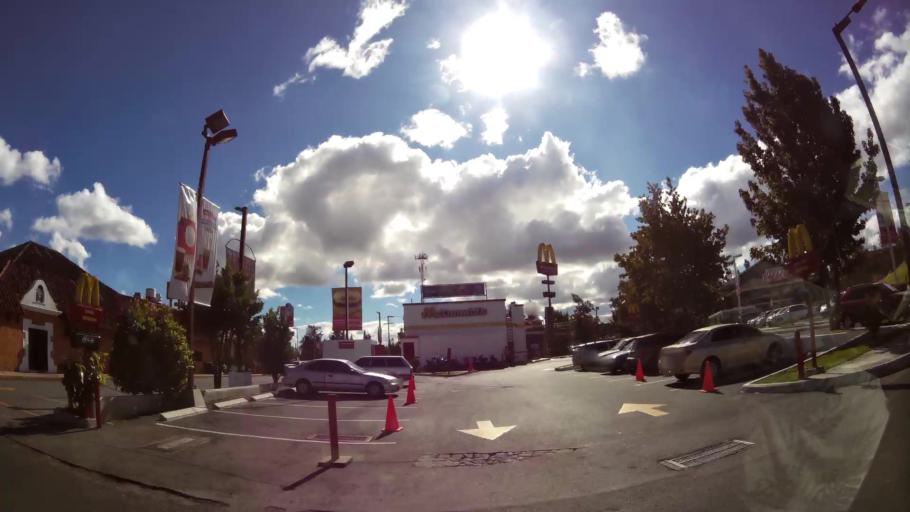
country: GT
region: Guatemala
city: Guatemala City
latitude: 14.6200
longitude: -90.5557
